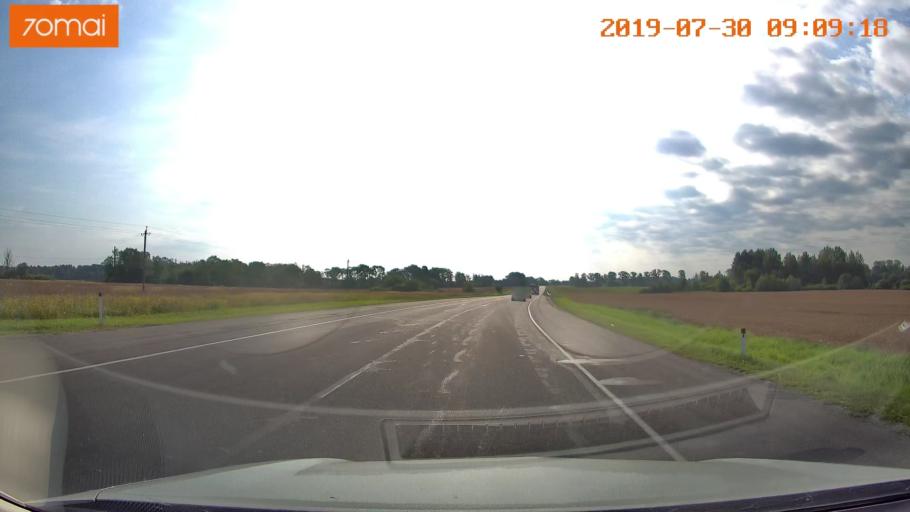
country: RU
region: Kaliningrad
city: Nesterov
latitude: 54.6138
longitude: 22.4067
